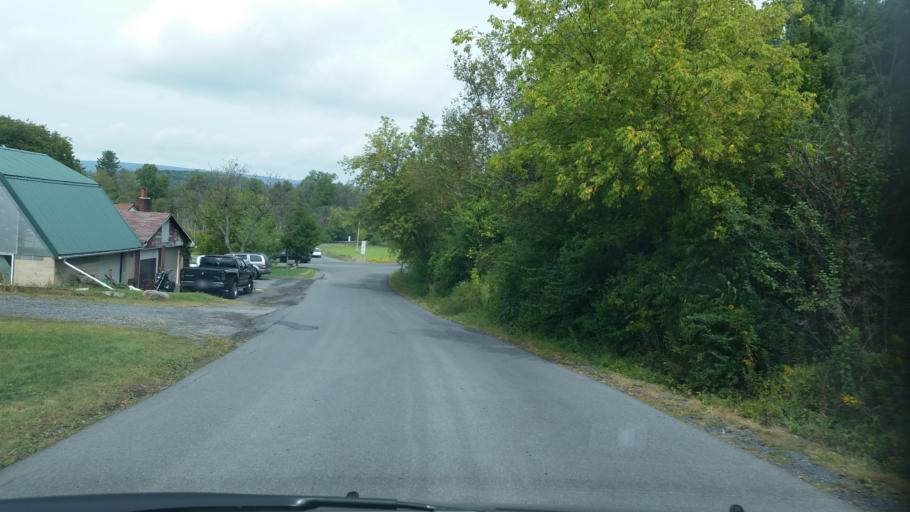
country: US
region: Pennsylvania
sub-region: Centre County
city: Centre Hall
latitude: 40.7970
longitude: -77.6427
